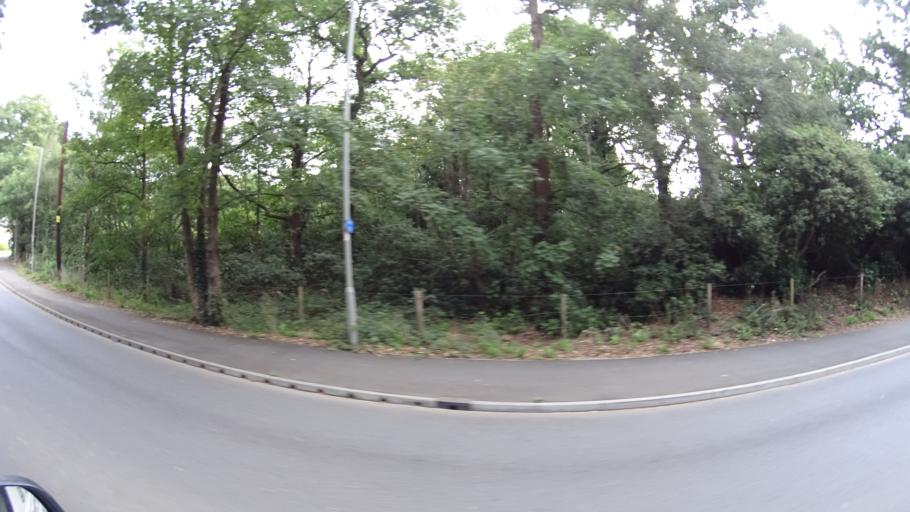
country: GB
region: England
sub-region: Dorset
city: Christchurch
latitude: 50.7715
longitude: -1.8210
